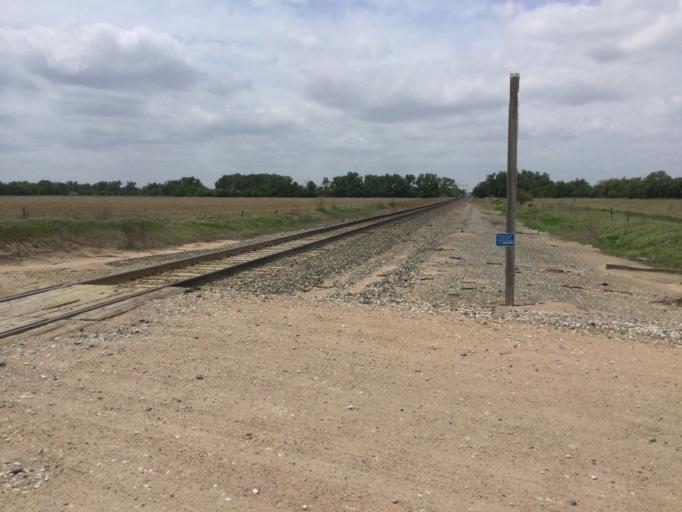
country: US
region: Kansas
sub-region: Edwards County
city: Kinsley
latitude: 37.9321
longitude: -99.3867
